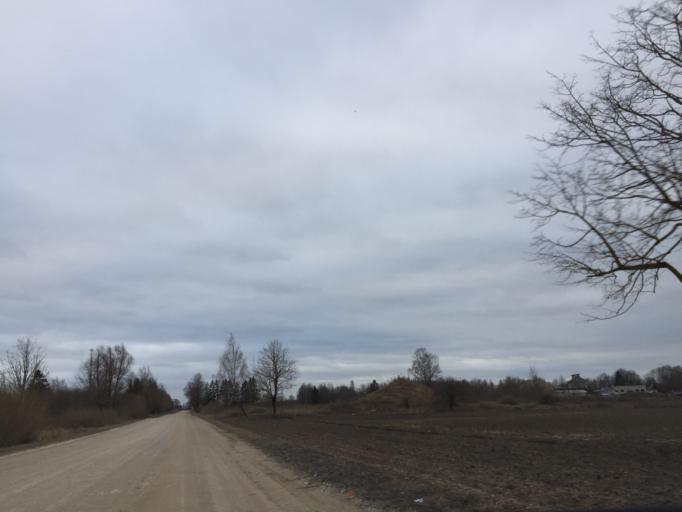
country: LT
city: Zagare
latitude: 56.3535
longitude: 23.2557
